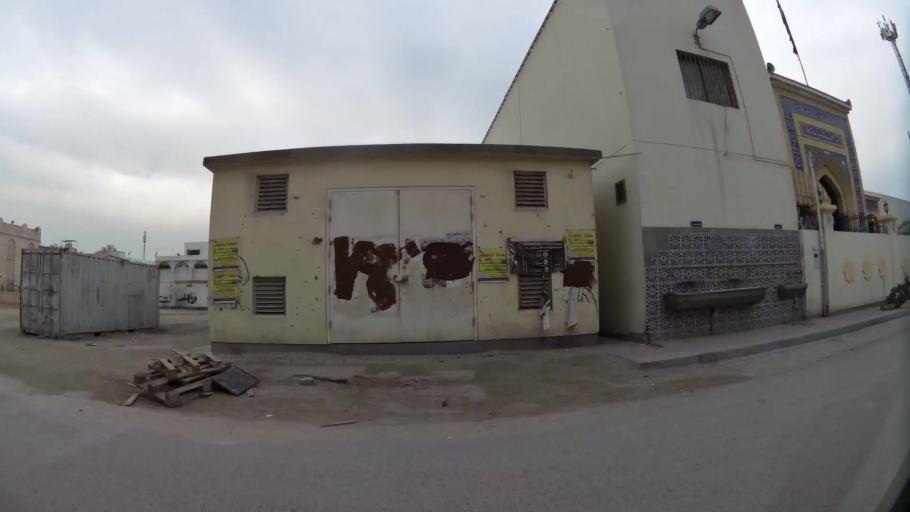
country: BH
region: Northern
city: Sitrah
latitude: 26.1337
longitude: 50.6136
